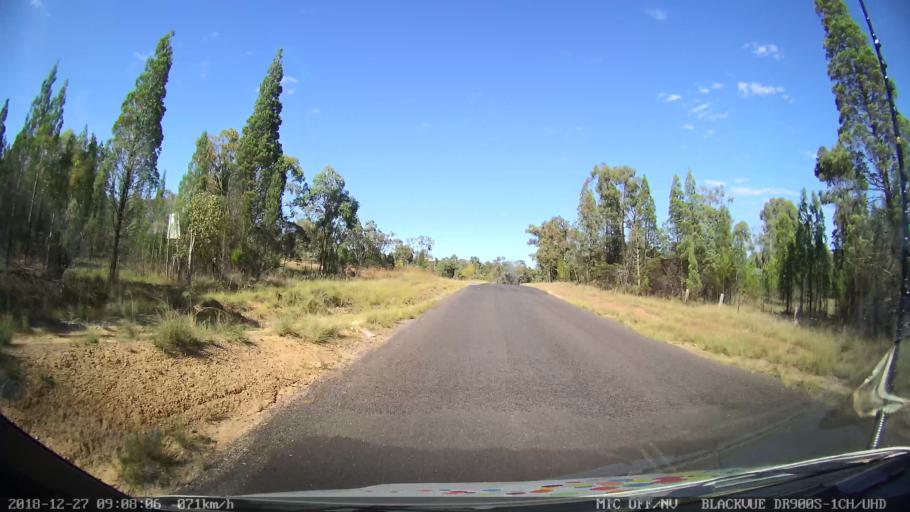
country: AU
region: New South Wales
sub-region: Lithgow
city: Portland
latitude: -33.1338
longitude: 150.1514
